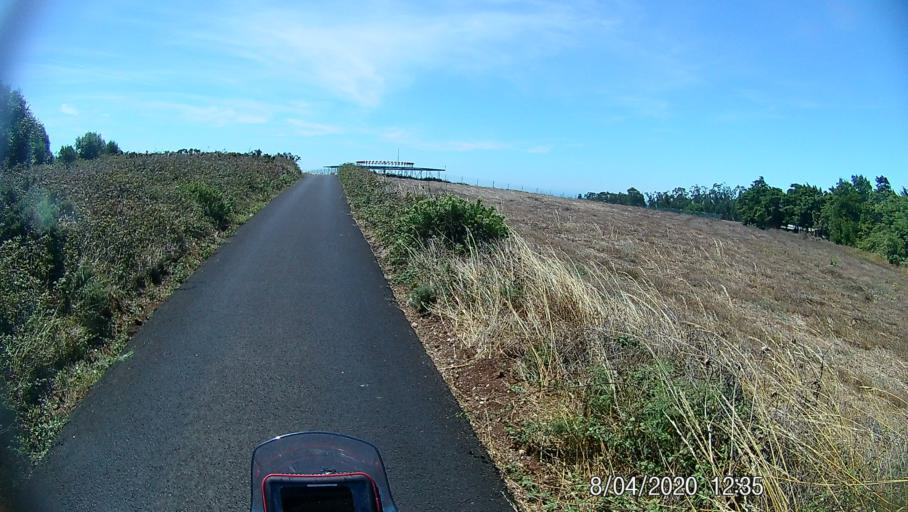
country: PT
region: Lisbon
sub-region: Sintra
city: Rio de Mouro
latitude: 38.7494
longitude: -9.3619
